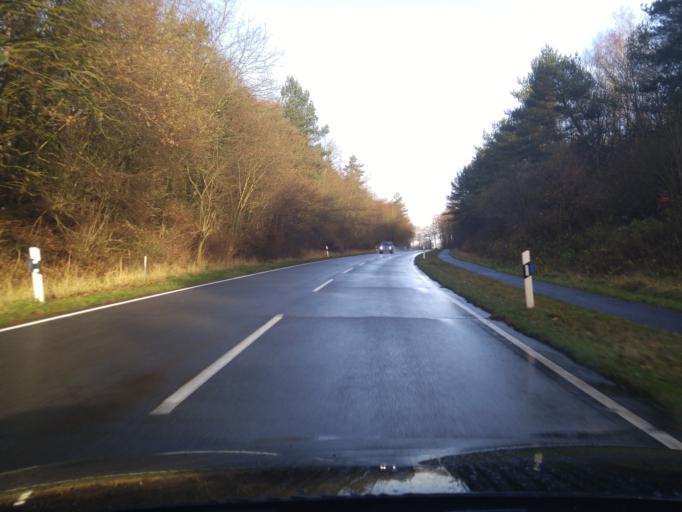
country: DE
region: Schleswig-Holstein
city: Ratekau
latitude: 53.9352
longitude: 10.7340
